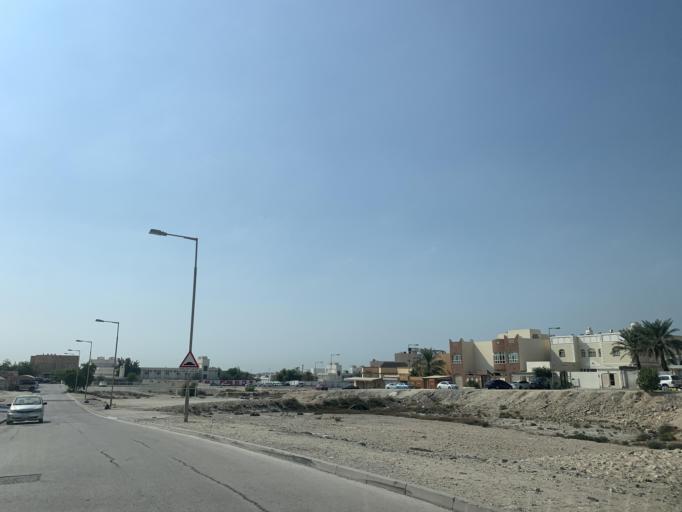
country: BH
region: Central Governorate
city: Madinat Hamad
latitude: 26.1141
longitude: 50.5026
